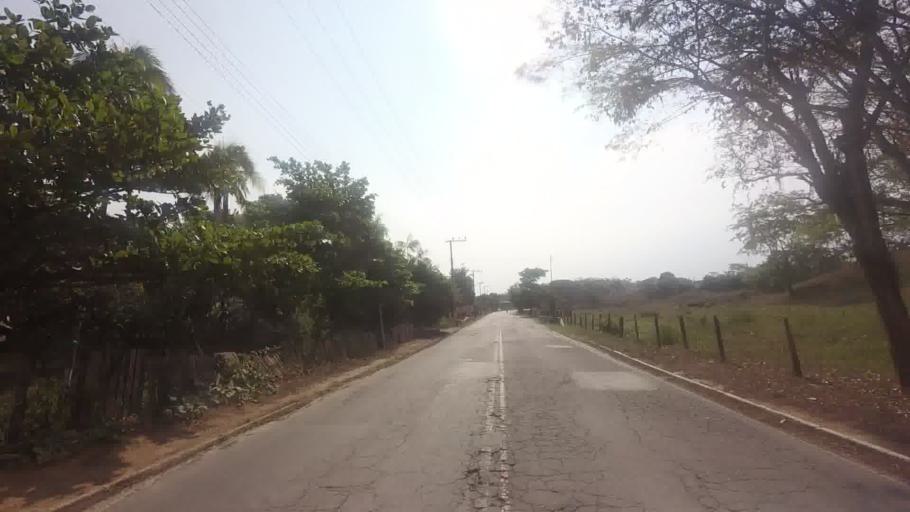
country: BR
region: Rio de Janeiro
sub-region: Bom Jesus Do Itabapoana
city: Bom Jesus do Itabapoana
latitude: -21.1459
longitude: -41.6226
